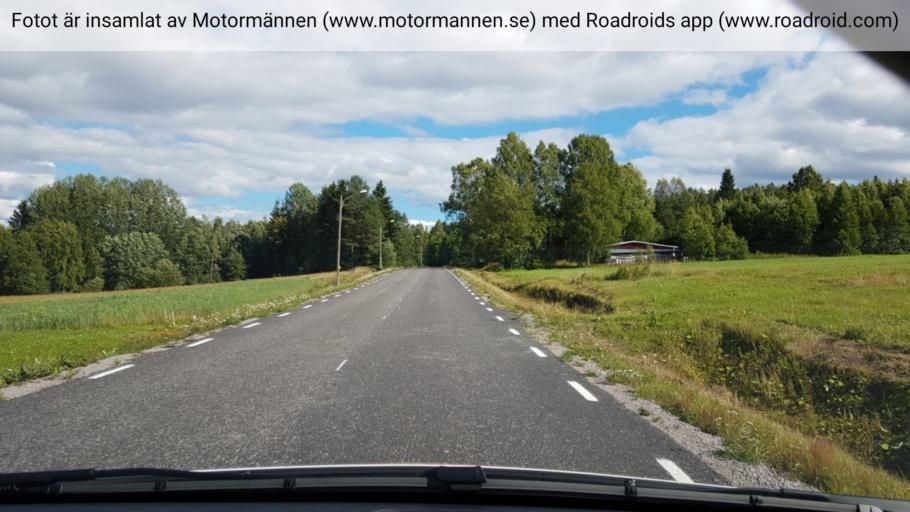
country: SE
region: Vaesterbotten
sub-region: Umea Kommun
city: Hoernefors
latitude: 63.7025
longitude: 19.7983
